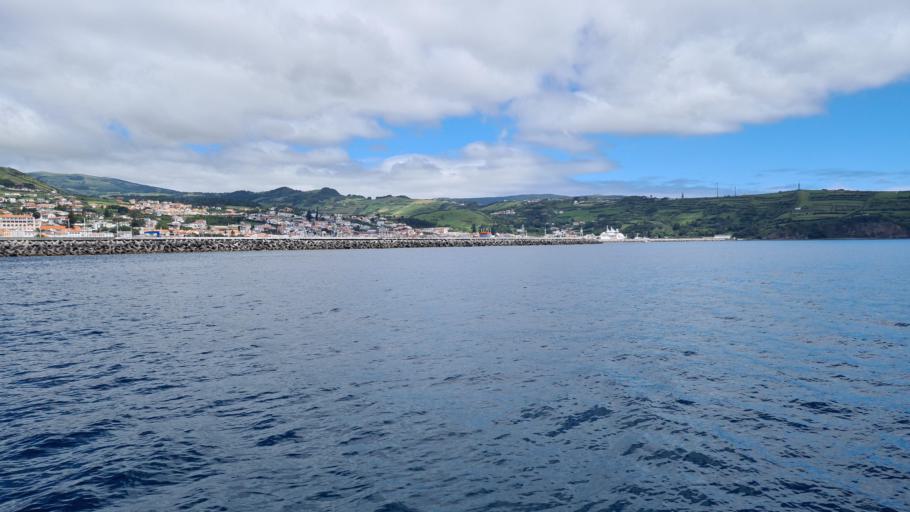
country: PT
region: Azores
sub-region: Horta
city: Horta
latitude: 38.5259
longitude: -28.6198
